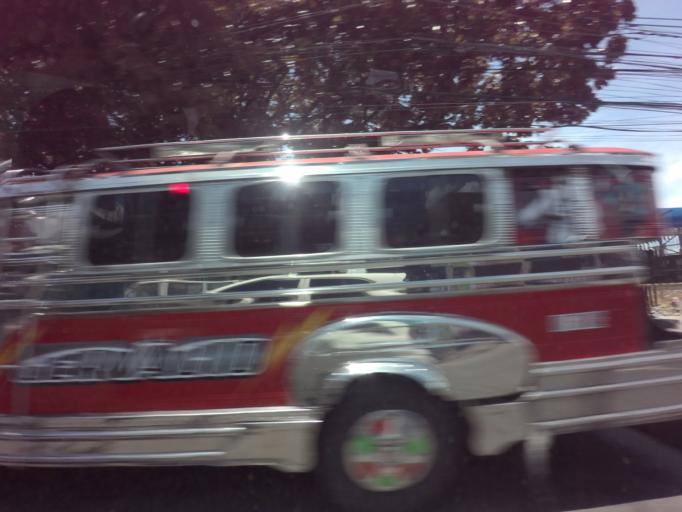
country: PH
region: Metro Manila
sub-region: Makati City
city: Makati City
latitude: 14.5079
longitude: 121.0318
